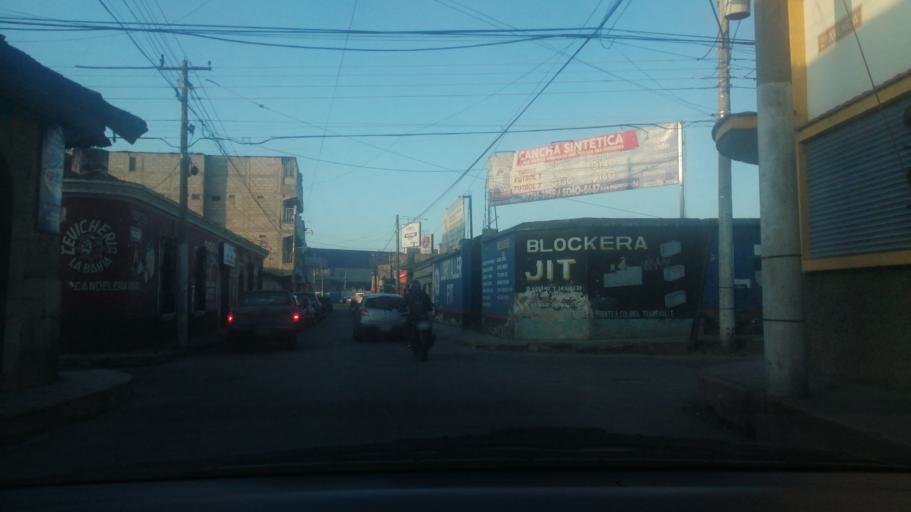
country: GT
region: Quetzaltenango
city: Quetzaltenango
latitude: 14.8336
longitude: -91.5125
